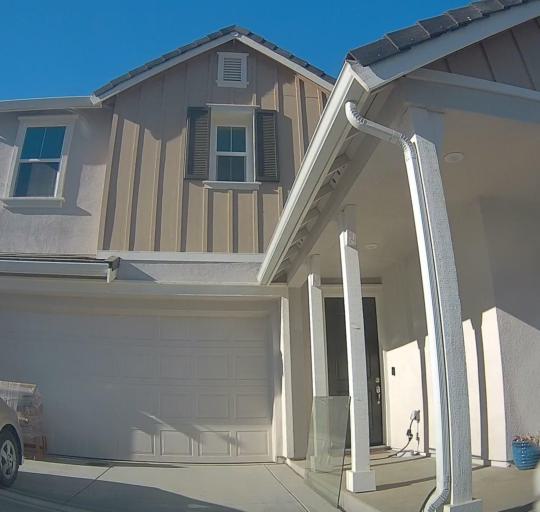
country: US
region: California
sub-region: Santa Clara County
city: Gilroy
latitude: 36.9936
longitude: -121.5922
